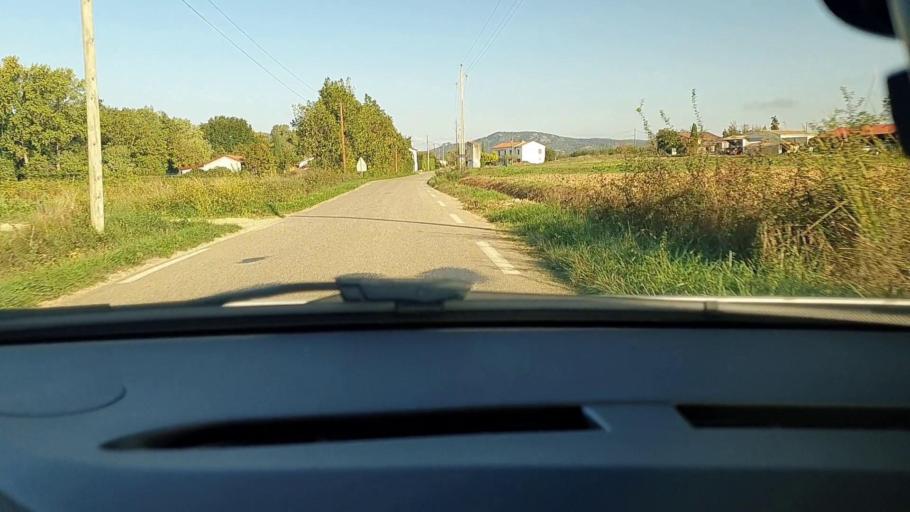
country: FR
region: Languedoc-Roussillon
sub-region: Departement du Gard
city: Saint-Ambroix
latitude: 44.2670
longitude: 4.2775
